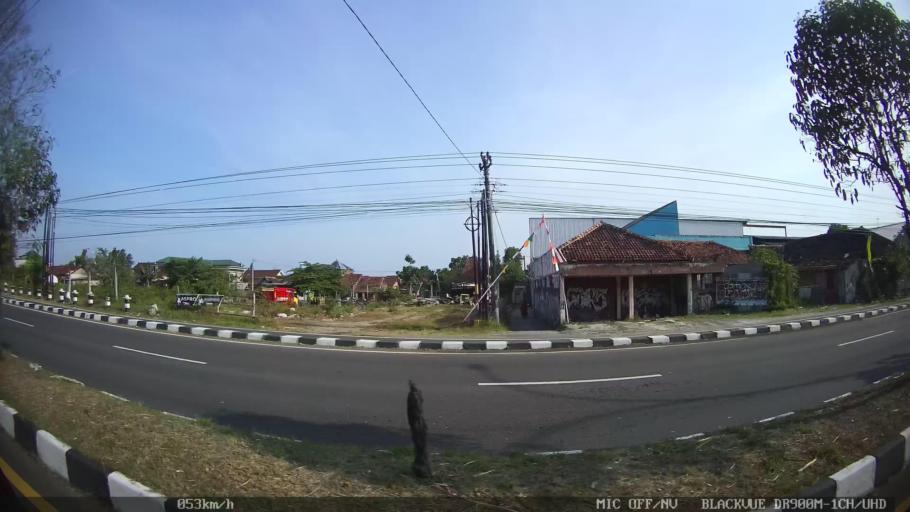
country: ID
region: Daerah Istimewa Yogyakarta
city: Kasihan
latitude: -7.8273
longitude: 110.3496
